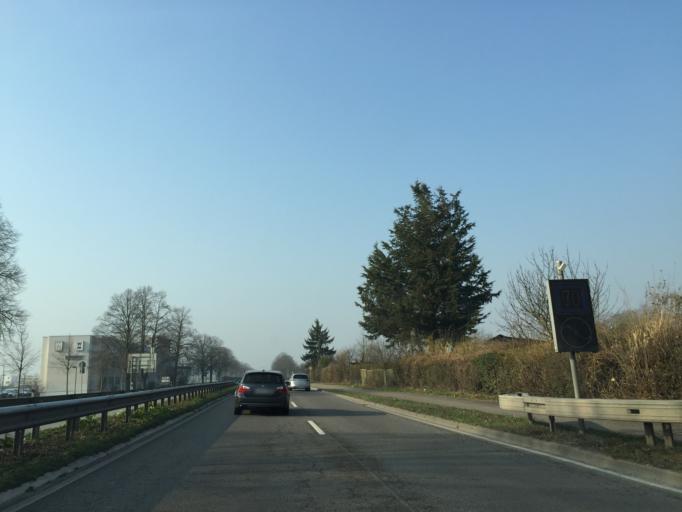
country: DE
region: Baden-Wuerttemberg
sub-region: Karlsruhe Region
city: Eppelheim
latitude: 49.3883
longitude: 8.6609
